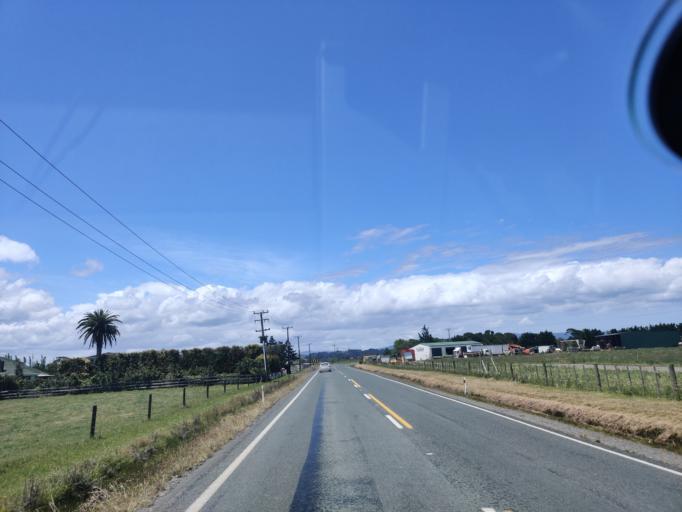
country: NZ
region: Northland
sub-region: Far North District
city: Kaitaia
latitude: -35.0291
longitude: 173.2530
